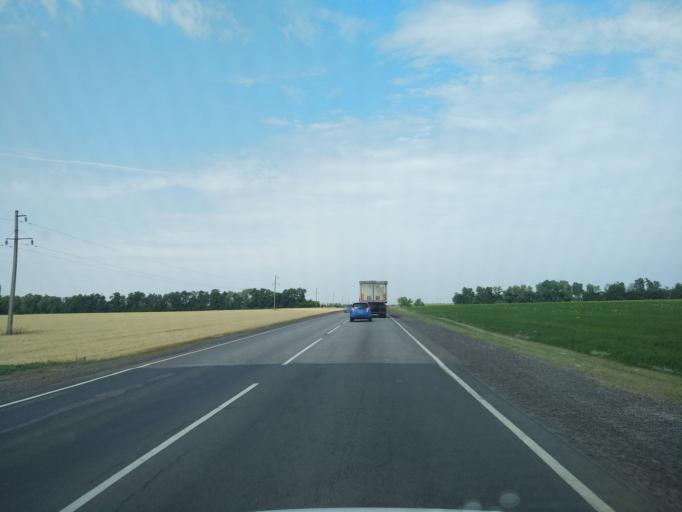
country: RU
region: Voronezj
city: Orlovo
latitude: 51.6832
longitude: 39.5598
